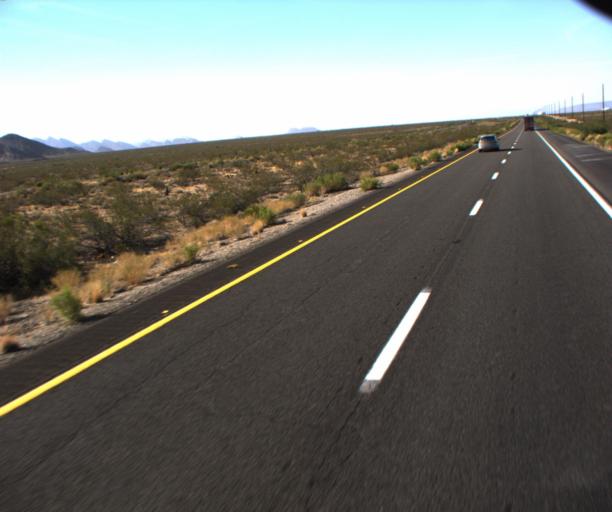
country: US
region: Arizona
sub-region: Mohave County
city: Kingman
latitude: 35.0880
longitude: -114.1206
